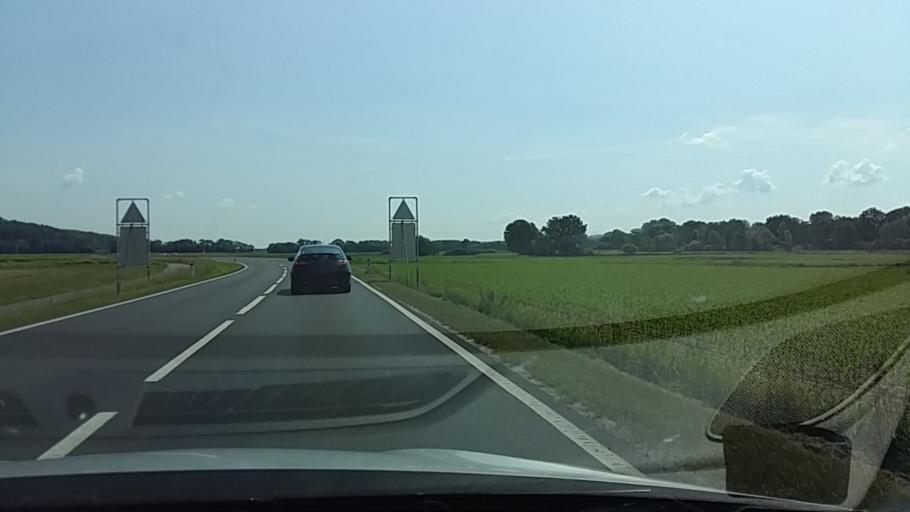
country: AT
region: Burgenland
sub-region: Politischer Bezirk Jennersdorf
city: Weichselbaum
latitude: 46.9435
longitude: 16.1951
